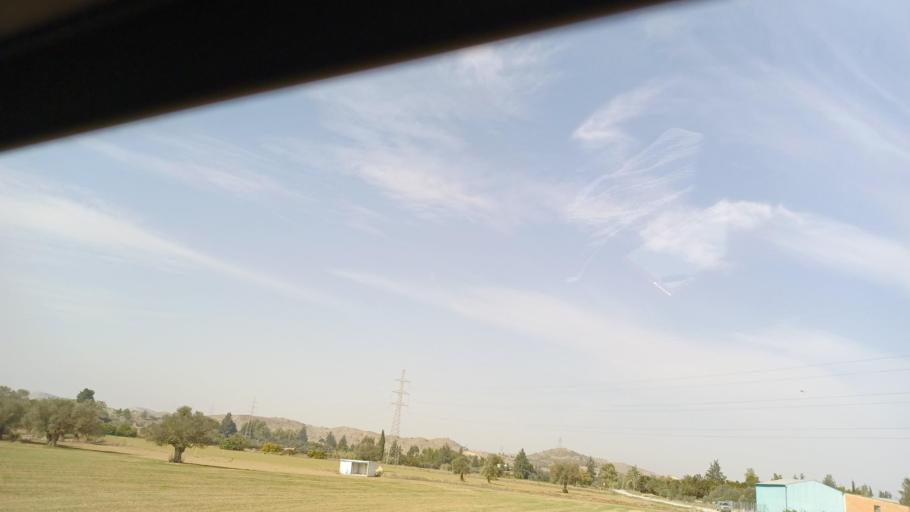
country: CY
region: Larnaka
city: Mosfiloti
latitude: 34.9700
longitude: 33.4464
